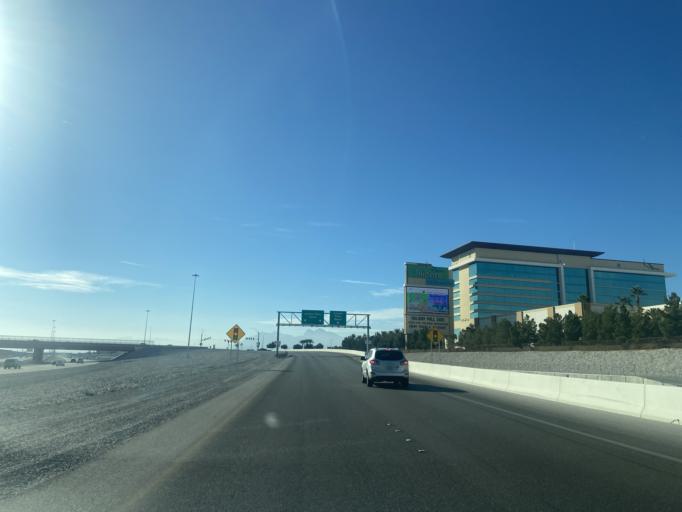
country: US
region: Nevada
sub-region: Clark County
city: North Las Vegas
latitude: 36.2917
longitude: -115.1779
